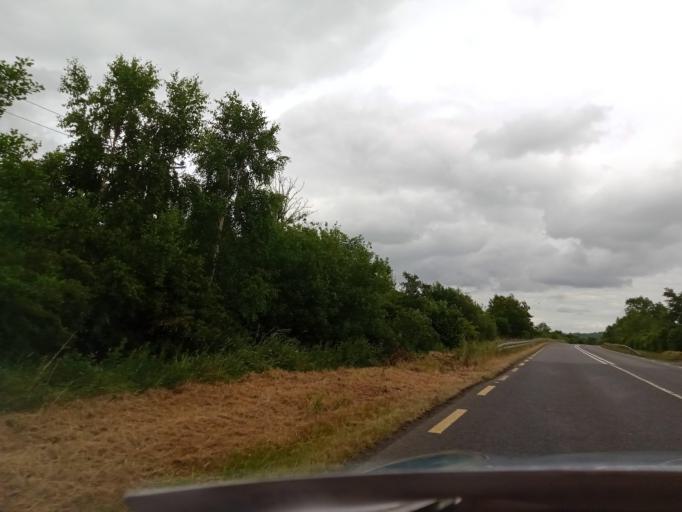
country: IE
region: Leinster
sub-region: Kilkenny
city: Thomastown
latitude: 52.4863
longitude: -7.2355
